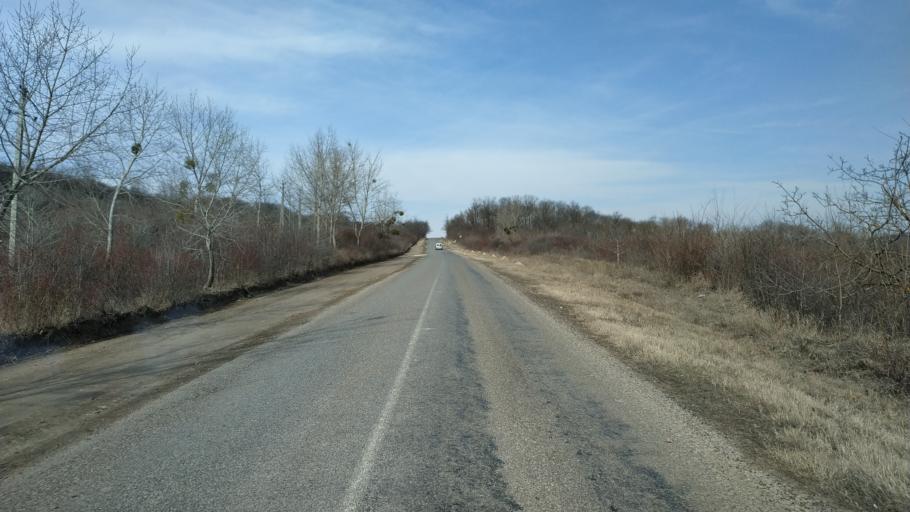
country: MD
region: Nisporeni
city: Nisporeni
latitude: 47.1883
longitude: 28.0704
